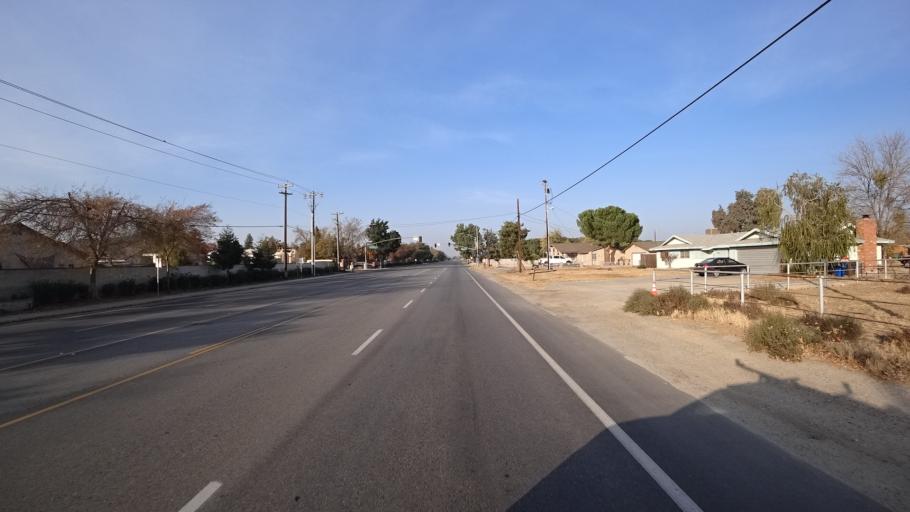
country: US
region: California
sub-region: Kern County
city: Greenacres
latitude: 35.3689
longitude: -119.1179
